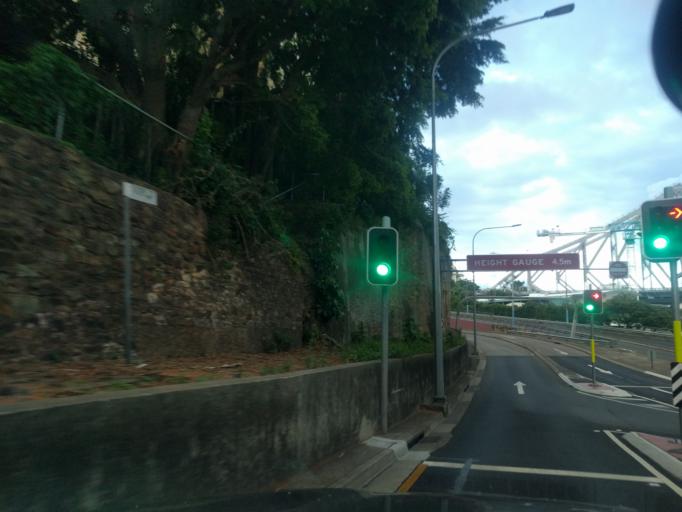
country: AU
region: Queensland
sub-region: Brisbane
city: Fortitude Valley
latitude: -27.4621
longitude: 153.0332
